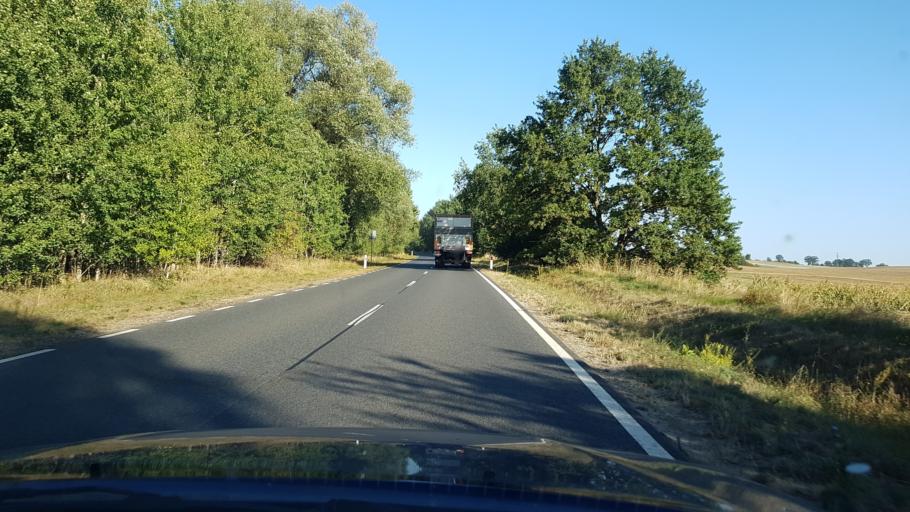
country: PL
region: West Pomeranian Voivodeship
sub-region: Powiat stargardzki
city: Marianowo
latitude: 53.4303
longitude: 15.2178
